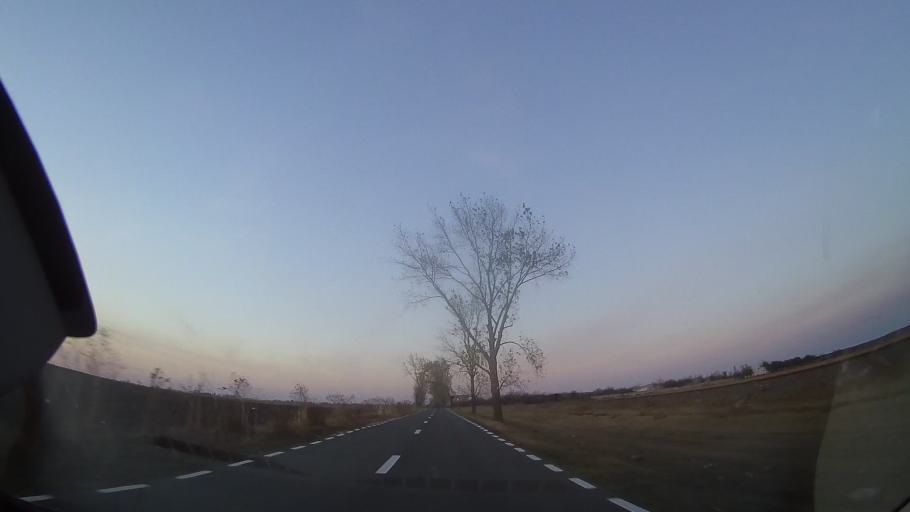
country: RO
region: Constanta
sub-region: Comuna Cobadin
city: Cobadin
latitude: 44.0425
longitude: 28.2553
